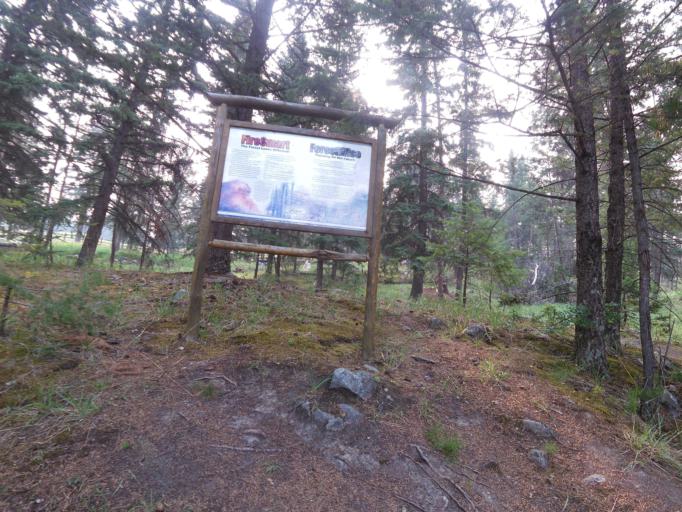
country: CA
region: Alberta
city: Jasper Park Lodge
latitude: 52.8825
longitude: -118.0536
